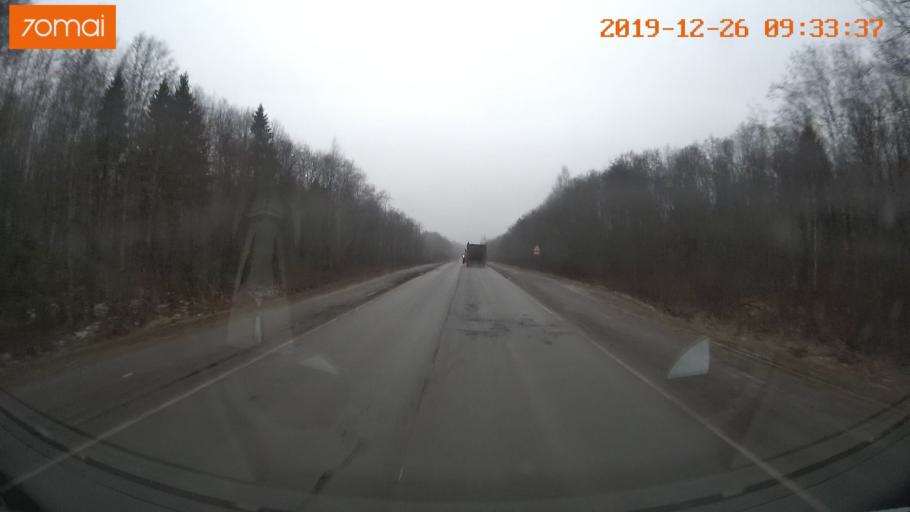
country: RU
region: Vologda
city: Vologda
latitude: 59.0919
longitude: 40.0978
